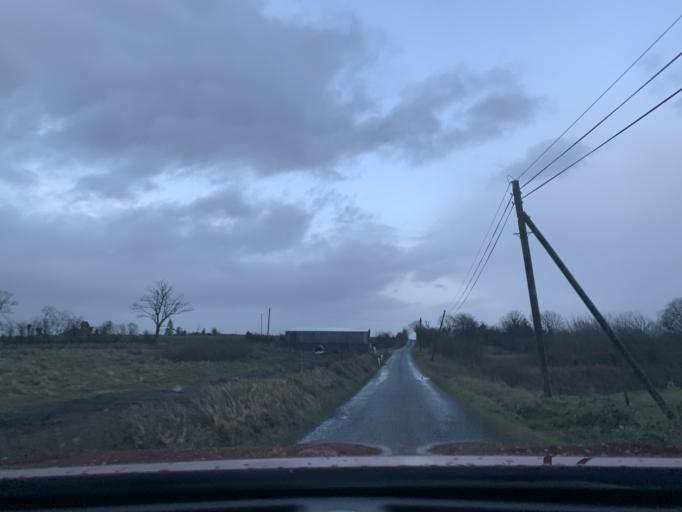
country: IE
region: Connaught
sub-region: Roscommon
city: Ballaghaderreen
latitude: 53.9828
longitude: -8.5405
